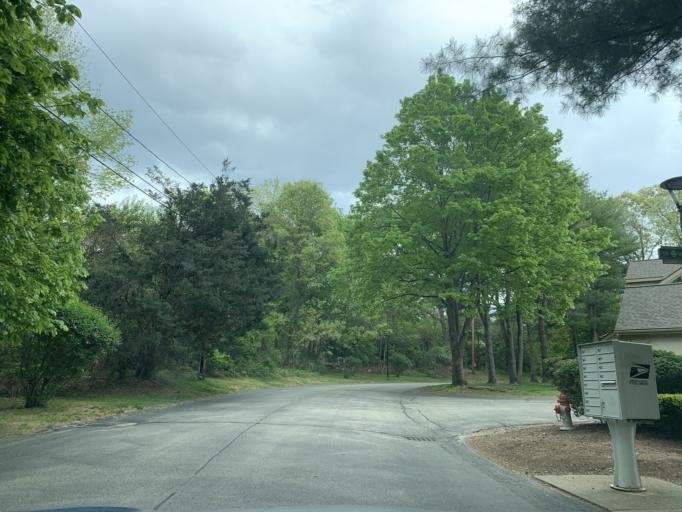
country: US
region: Rhode Island
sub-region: Kent County
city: East Greenwich
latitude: 41.6480
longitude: -71.4923
